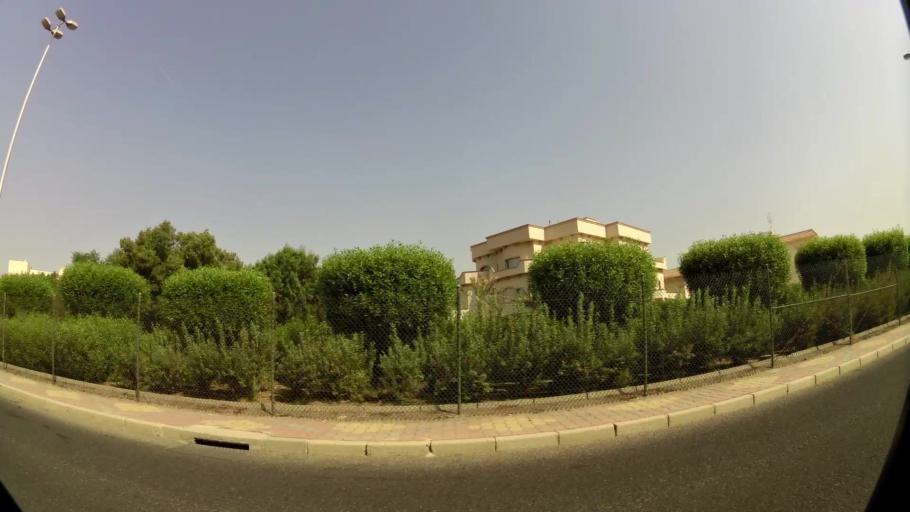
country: KW
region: Al Asimah
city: Ad Dasmah
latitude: 29.3539
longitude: 48.0073
